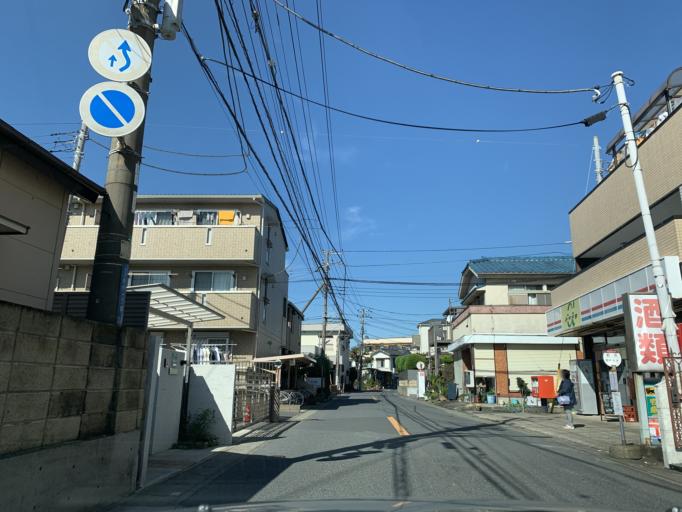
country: JP
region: Tokyo
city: Urayasu
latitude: 35.6748
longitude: 139.8921
